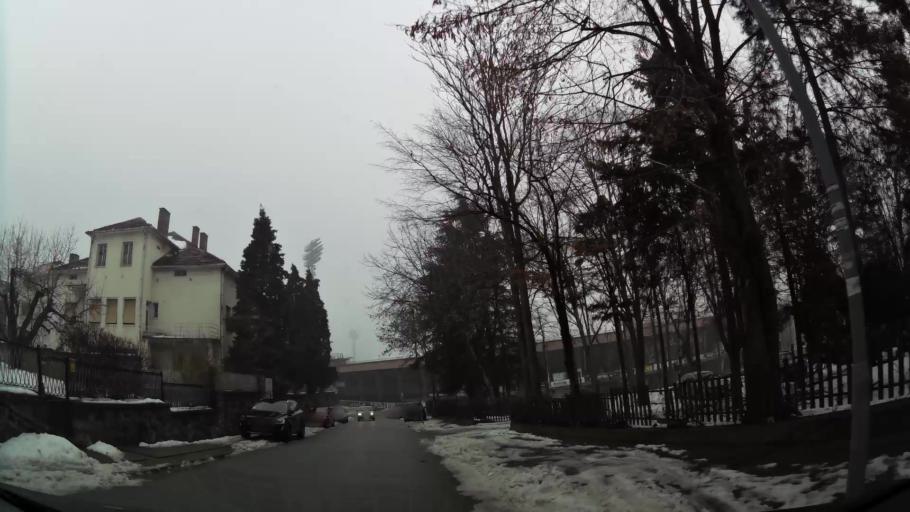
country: RS
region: Central Serbia
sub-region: Belgrade
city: Savski Venac
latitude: 44.7872
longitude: 20.4600
